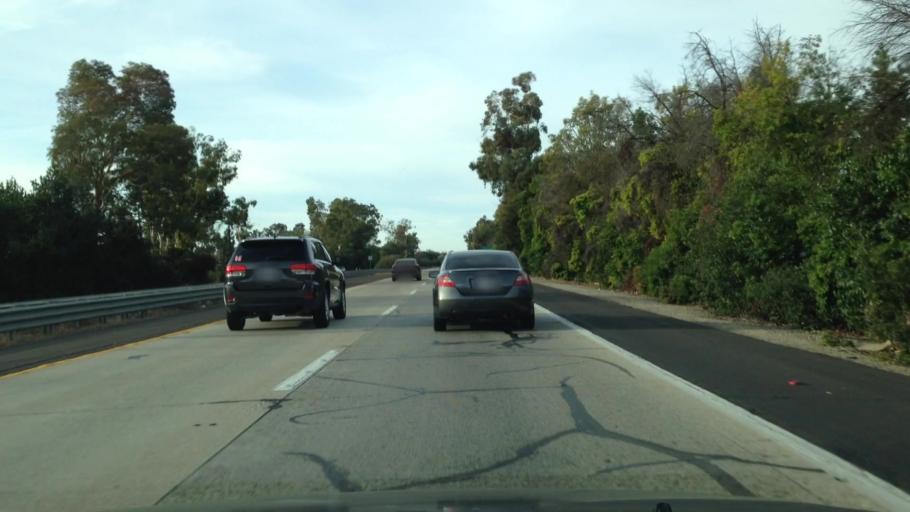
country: US
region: California
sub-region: Ventura County
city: Saticoy
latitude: 34.2804
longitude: -119.1722
